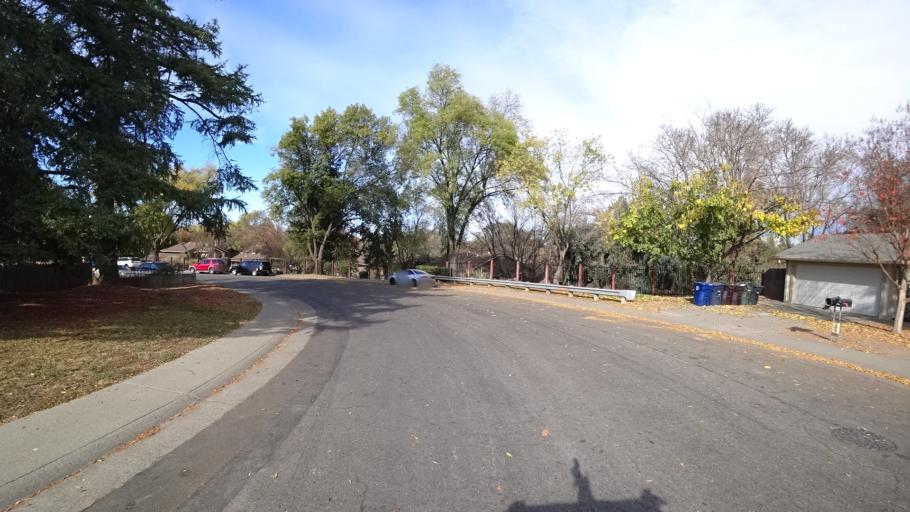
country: US
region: California
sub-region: Sacramento County
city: Citrus Heights
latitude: 38.6824
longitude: -121.2742
